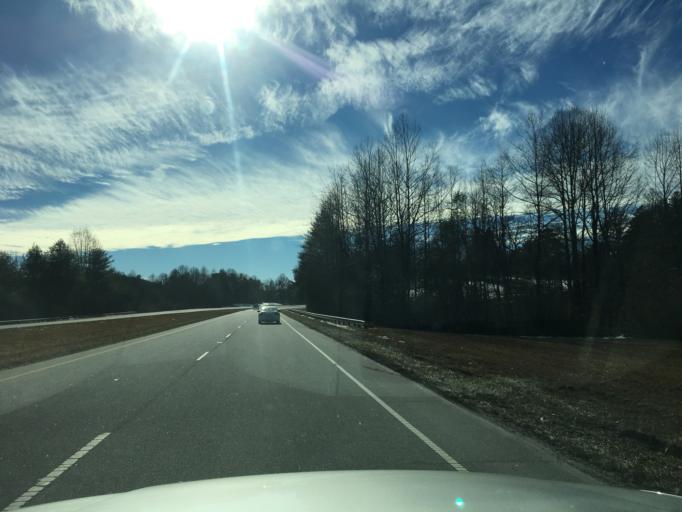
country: US
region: North Carolina
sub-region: Transylvania County
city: Brevard
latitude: 35.2067
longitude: -82.7658
